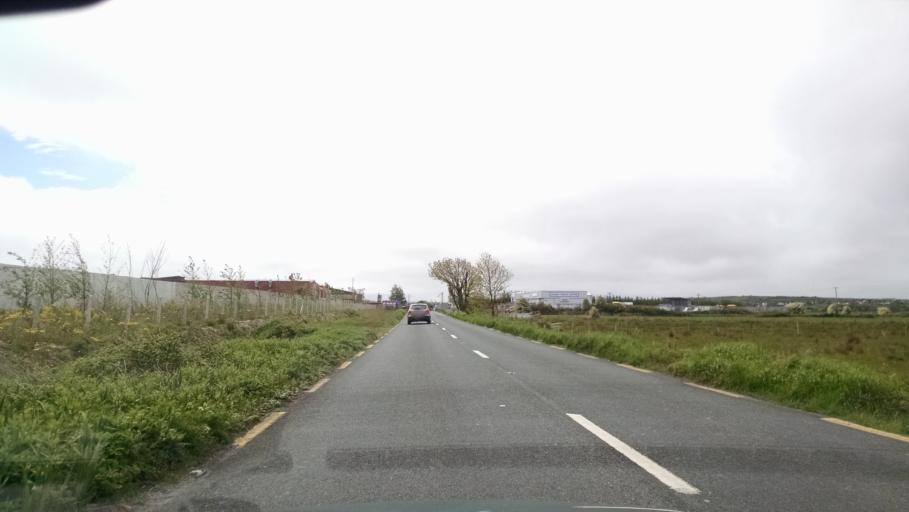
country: IE
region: Connaught
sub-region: County Galway
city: Gaillimh
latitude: 53.3344
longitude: -9.0201
